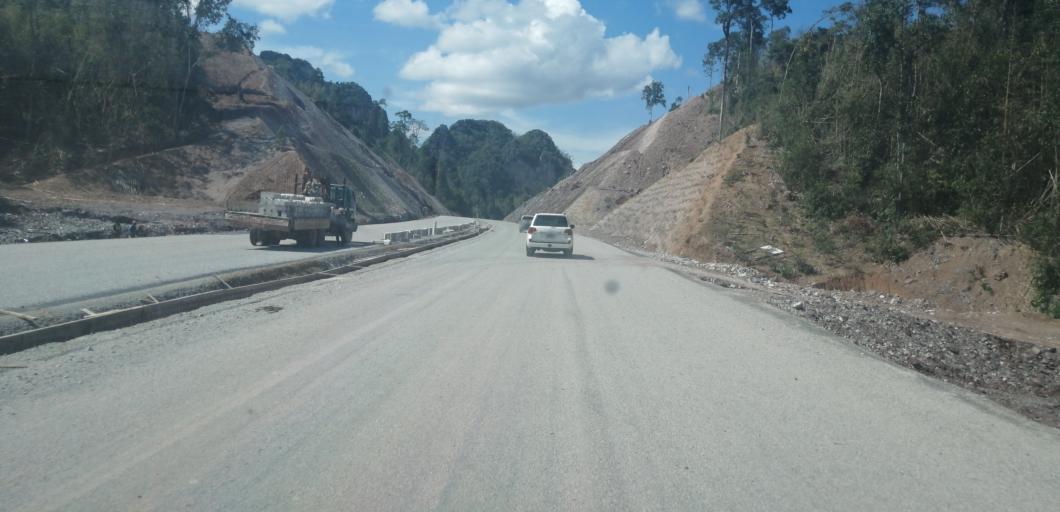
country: LA
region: Vientiane
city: Vangviang
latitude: 18.8589
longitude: 102.4218
